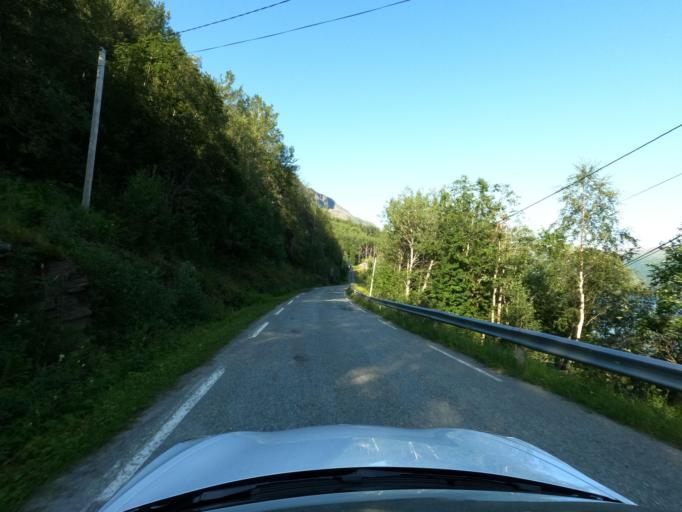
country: NO
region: Troms
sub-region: Gratangen
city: Gratangen
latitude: 68.5593
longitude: 17.6614
